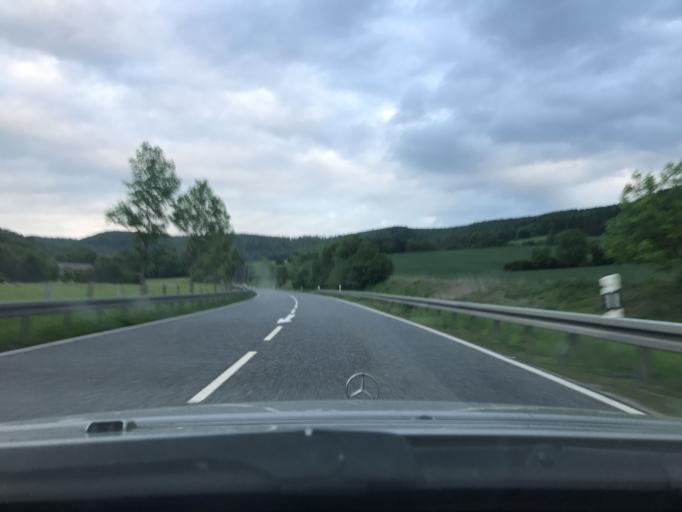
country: DE
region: Hesse
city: Wanfried
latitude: 51.1793
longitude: 10.1881
